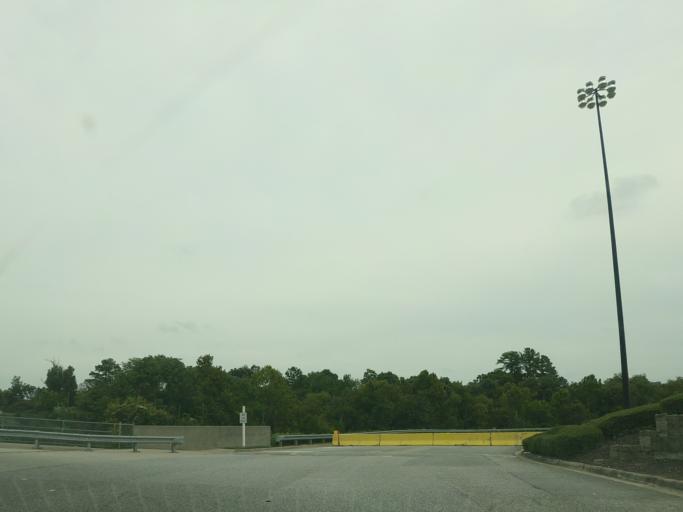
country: US
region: Georgia
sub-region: Bibb County
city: Macon
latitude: 32.8193
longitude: -83.6894
